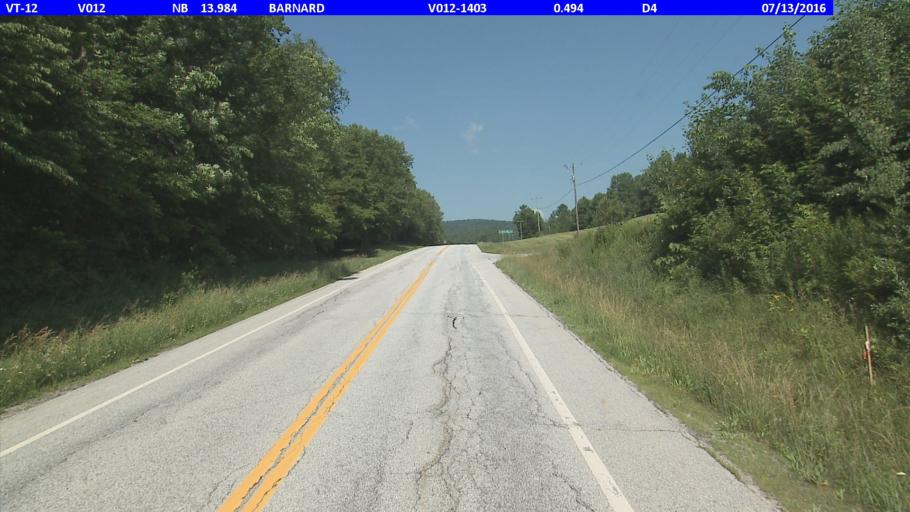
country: US
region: Vermont
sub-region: Windsor County
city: Woodstock
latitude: 43.6781
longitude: -72.5896
